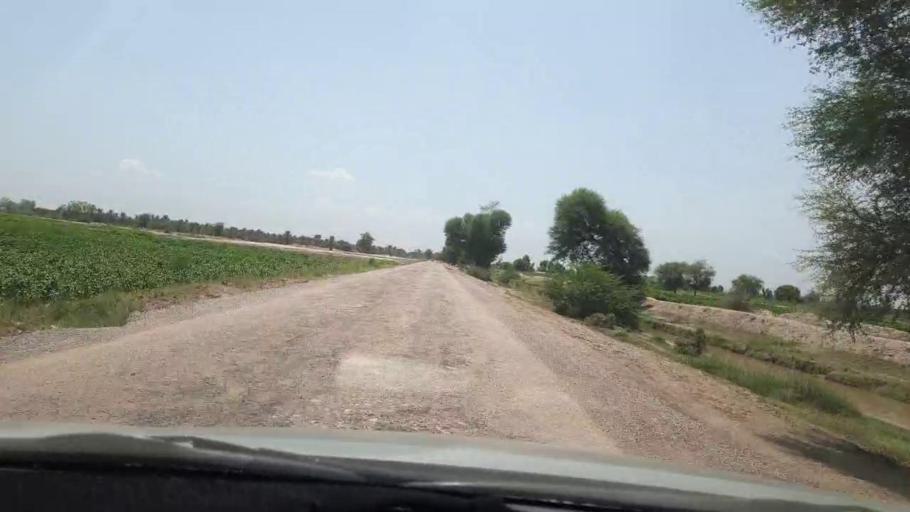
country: PK
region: Sindh
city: Pano Aqil
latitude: 27.7395
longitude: 69.1969
